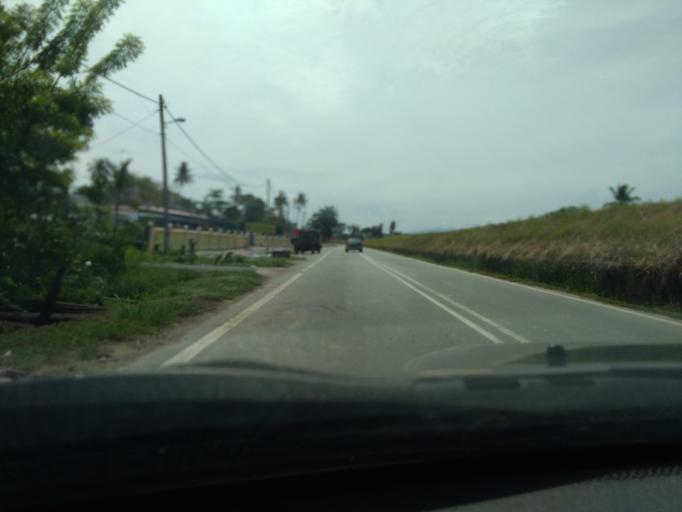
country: MY
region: Perak
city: Bagan Serai
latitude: 5.0138
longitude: 100.5359
